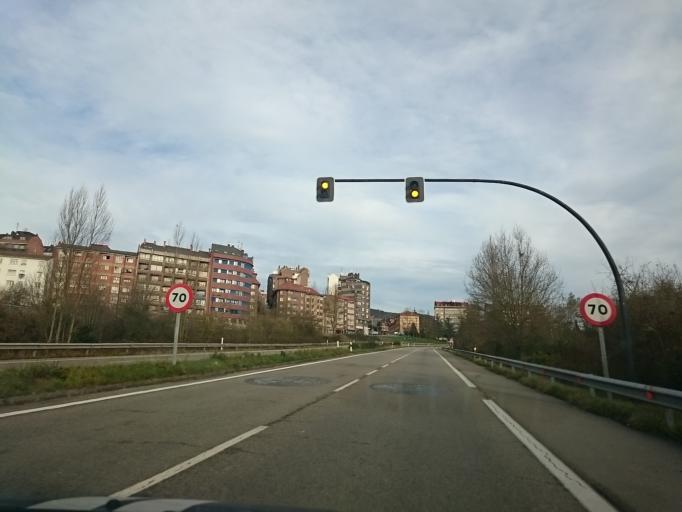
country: ES
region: Asturias
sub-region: Province of Asturias
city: Oviedo
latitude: 43.3519
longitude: -5.8561
